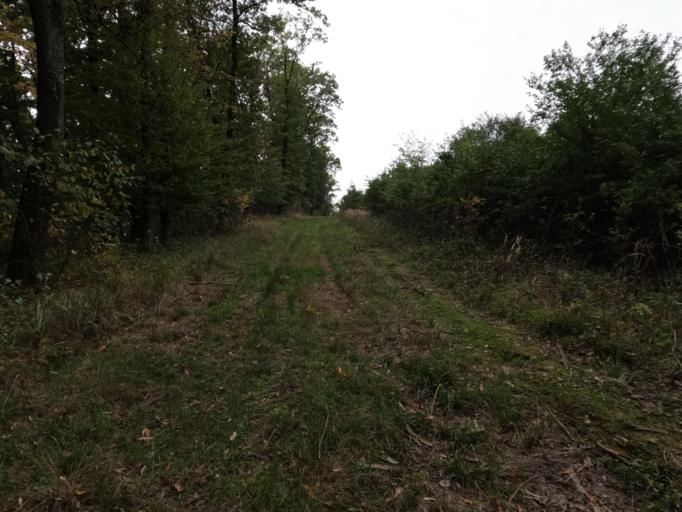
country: HU
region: Tolna
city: Szentgalpuszta
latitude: 46.3192
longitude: 18.6520
